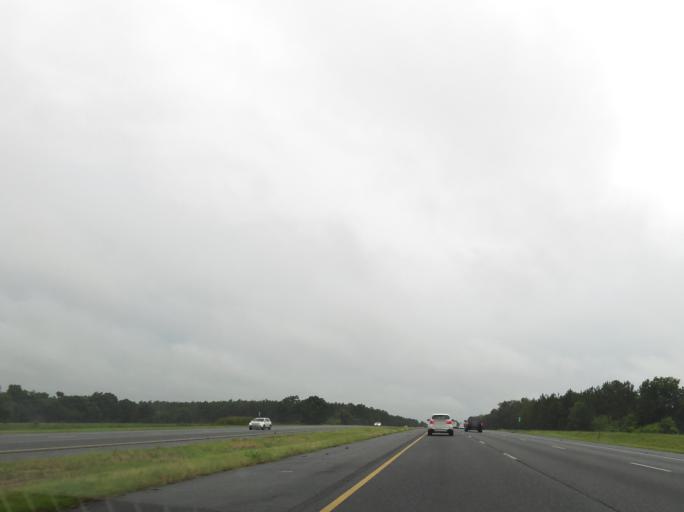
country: US
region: Georgia
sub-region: Crisp County
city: Cordele
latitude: 31.8828
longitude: -83.7287
